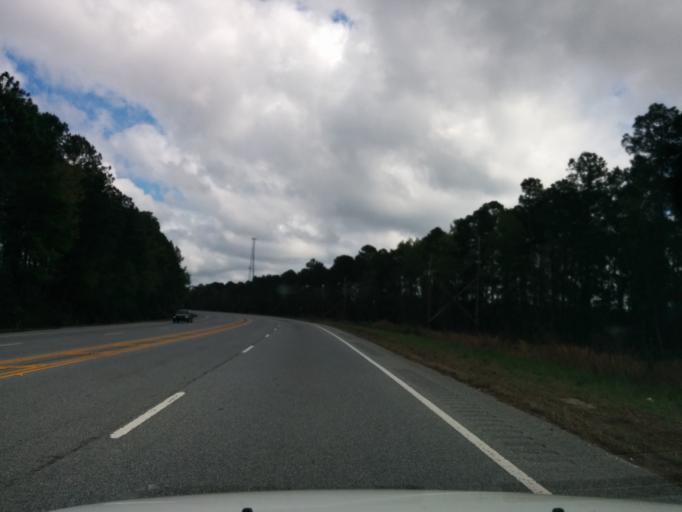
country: US
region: Georgia
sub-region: Glynn County
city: Brunswick
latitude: 31.1162
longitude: -81.5381
